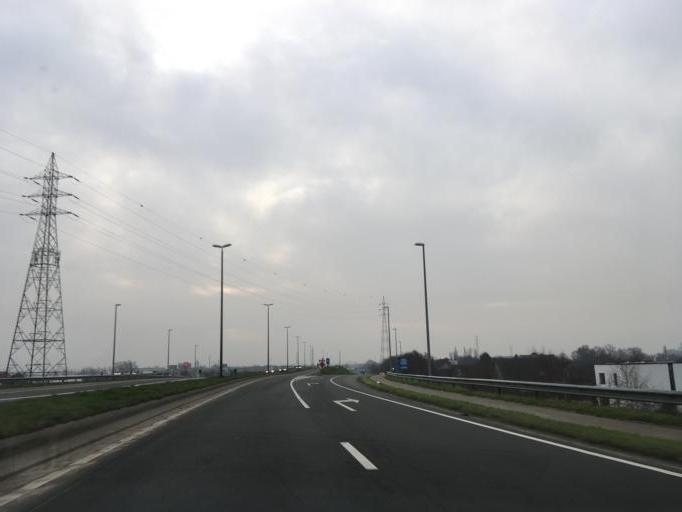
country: BE
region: Flanders
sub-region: Provincie West-Vlaanderen
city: Wielsbeke
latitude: 50.9006
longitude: 3.3952
